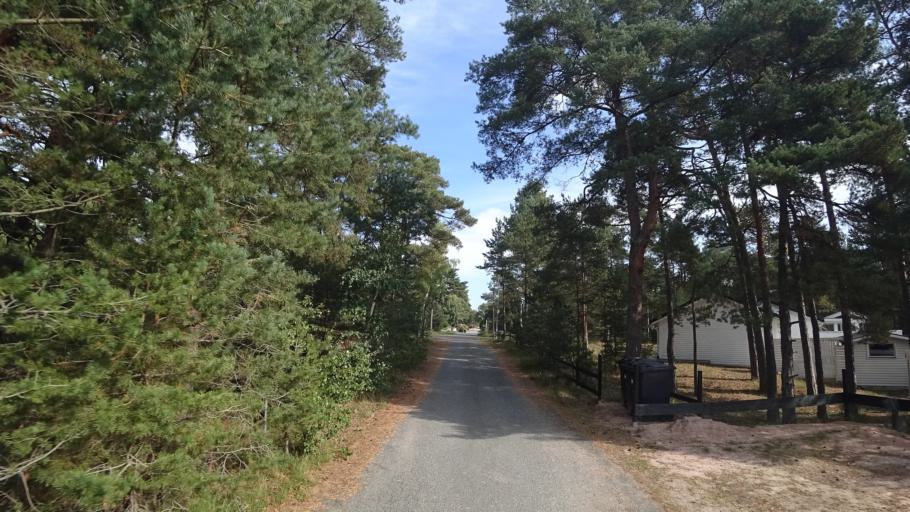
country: SE
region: Skane
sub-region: Kristianstads Kommun
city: Ahus
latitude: 55.9100
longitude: 14.2880
